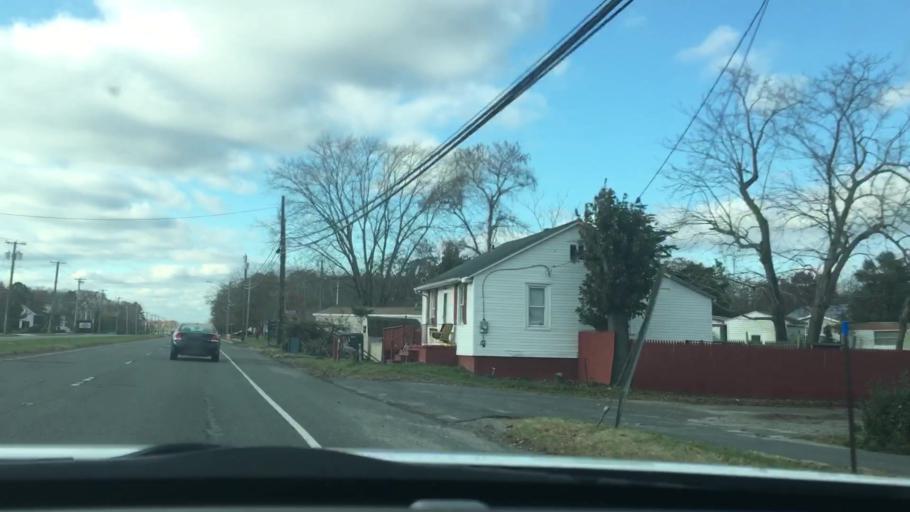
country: US
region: New Jersey
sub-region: Atlantic County
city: Northfield
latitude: 39.4126
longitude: -74.5723
